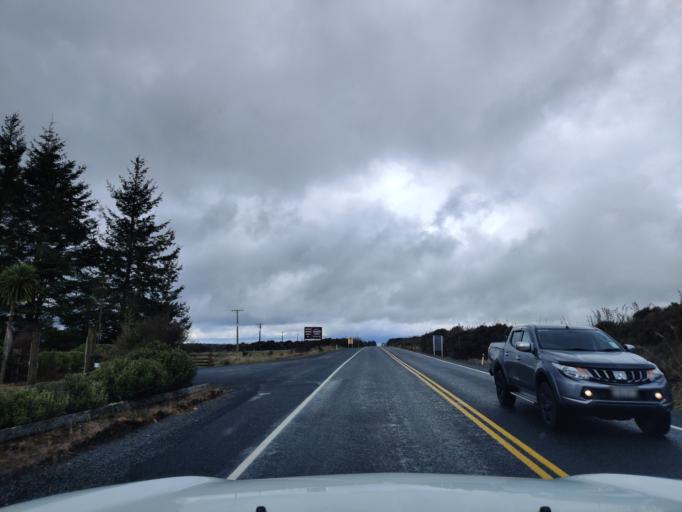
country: NZ
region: Manawatu-Wanganui
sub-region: Ruapehu District
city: Waiouru
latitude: -39.1968
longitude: 175.4013
